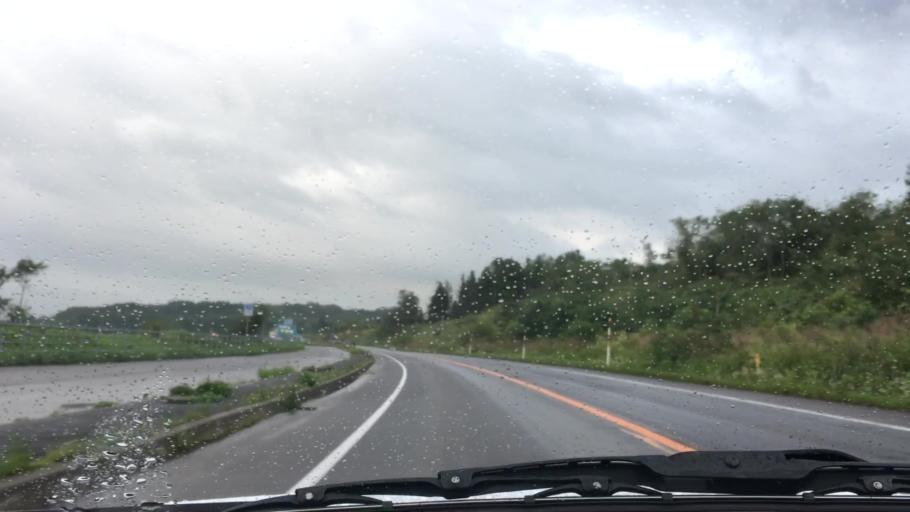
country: JP
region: Hokkaido
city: Nanae
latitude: 42.1811
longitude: 140.4397
